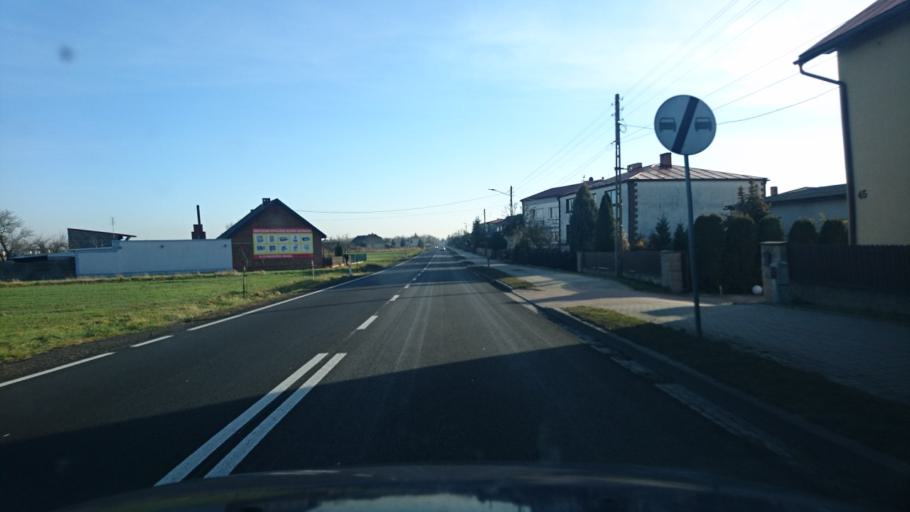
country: PL
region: Silesian Voivodeship
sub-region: Powiat klobucki
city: Starokrzepice
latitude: 51.0008
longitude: 18.6655
